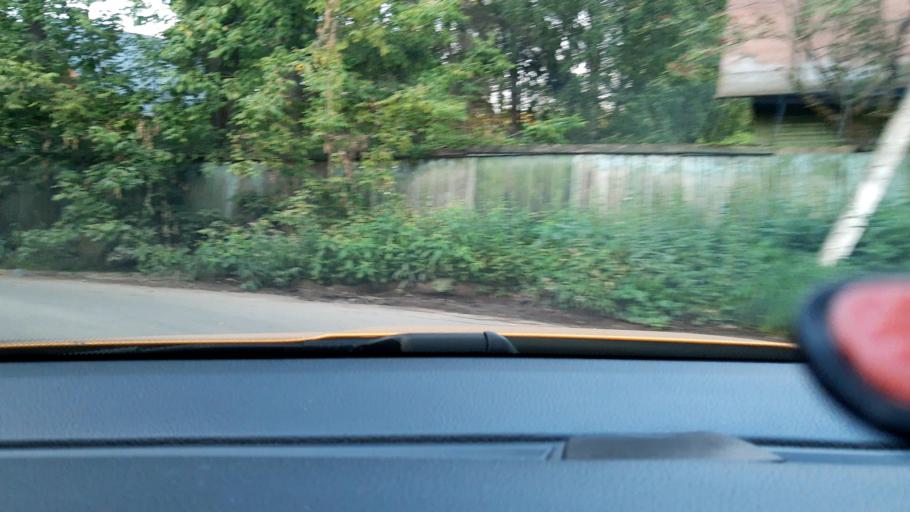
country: RU
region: Moscow
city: Novo-Peredelkino
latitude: 55.6657
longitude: 37.3420
